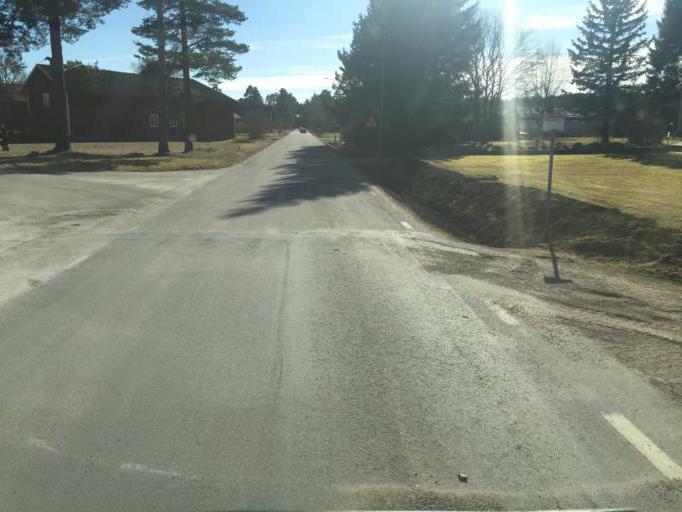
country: SE
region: Dalarna
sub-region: Vansbro Kommun
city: Vansbro
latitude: 60.4834
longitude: 14.0111
